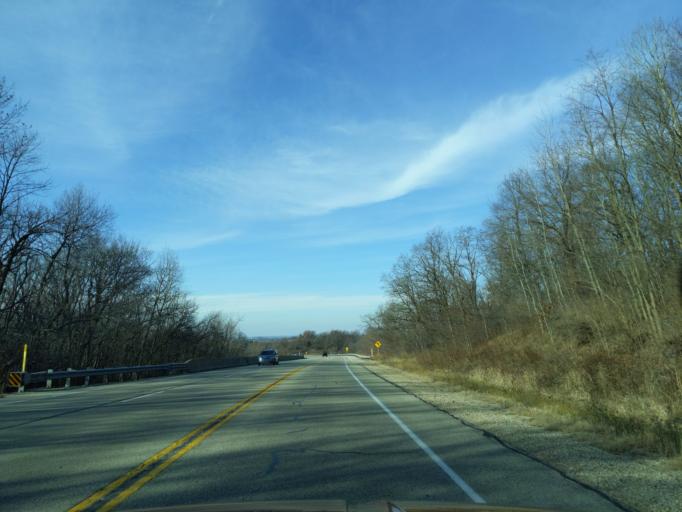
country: US
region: Wisconsin
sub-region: Walworth County
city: Whitewater
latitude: 42.8014
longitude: -88.6489
